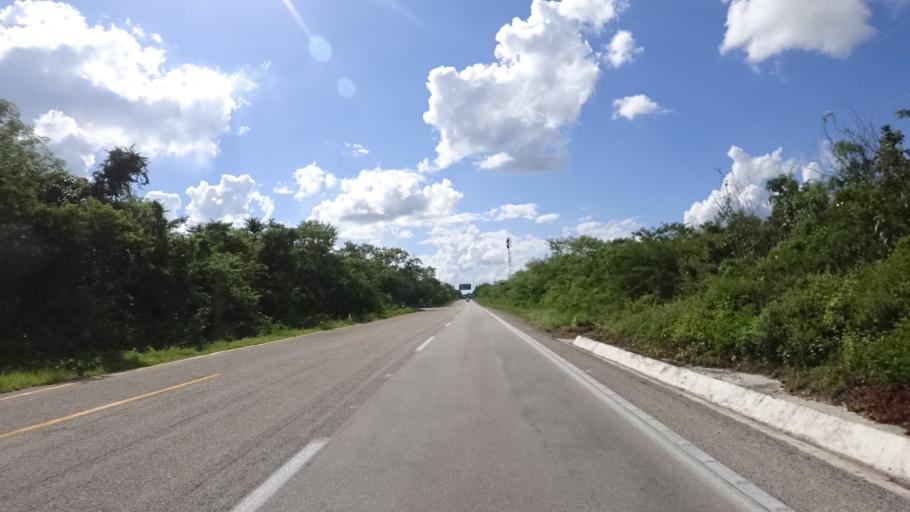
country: MX
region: Yucatan
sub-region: Kantunil
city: Kantunil
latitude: 20.8055
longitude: -89.0229
